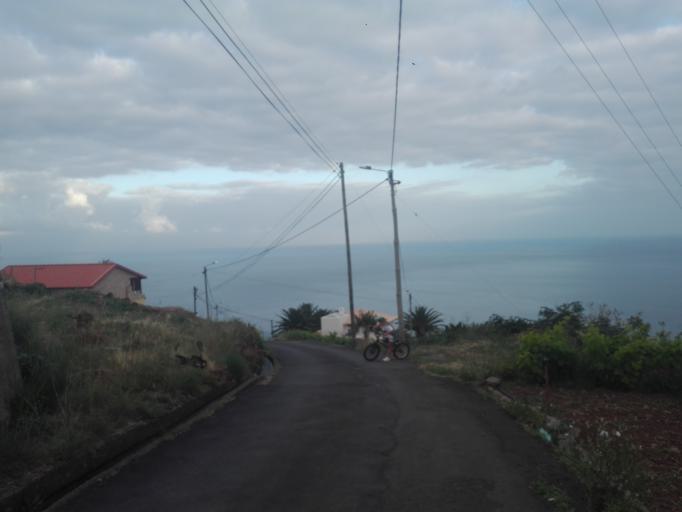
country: PT
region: Madeira
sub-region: Santa Cruz
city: Camacha
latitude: 32.6542
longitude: -16.8256
